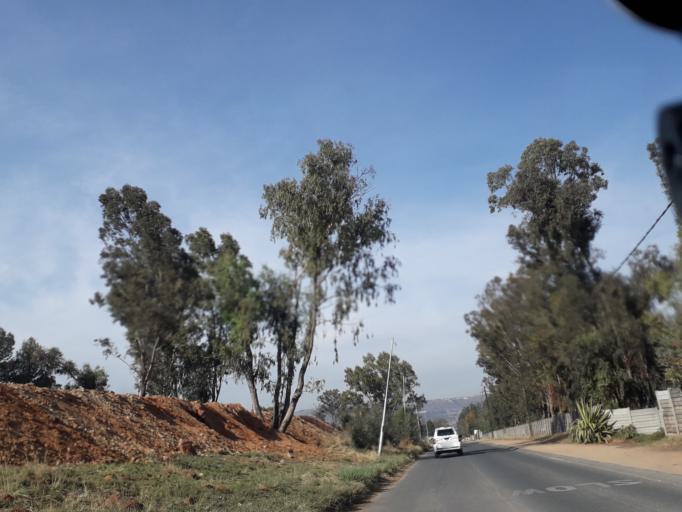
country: ZA
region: Gauteng
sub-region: West Rand District Municipality
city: Muldersdriseloop
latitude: -26.0650
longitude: 27.9037
